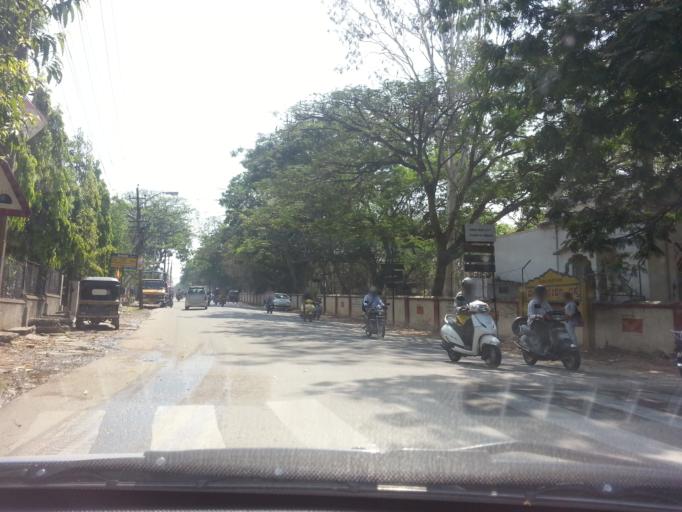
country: IN
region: Karnataka
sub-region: Mysore
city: Mysore
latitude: 12.3083
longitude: 76.6676
